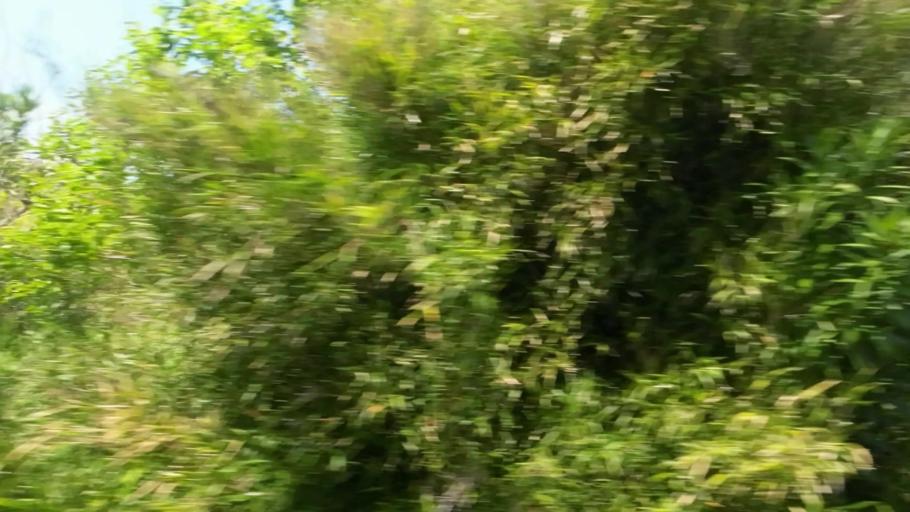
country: JP
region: Ehime
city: Hojo
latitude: 33.9670
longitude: 132.7738
